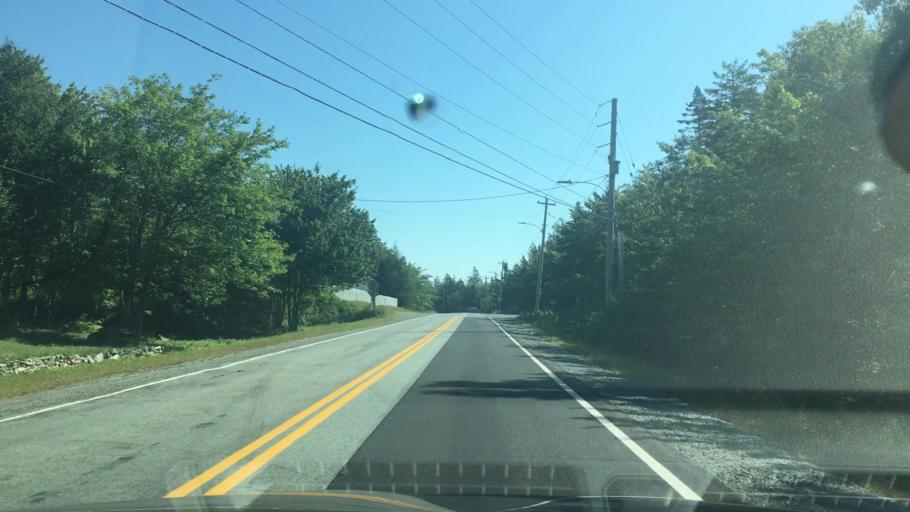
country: CA
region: Nova Scotia
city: New Glasgow
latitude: 44.9103
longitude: -62.5472
